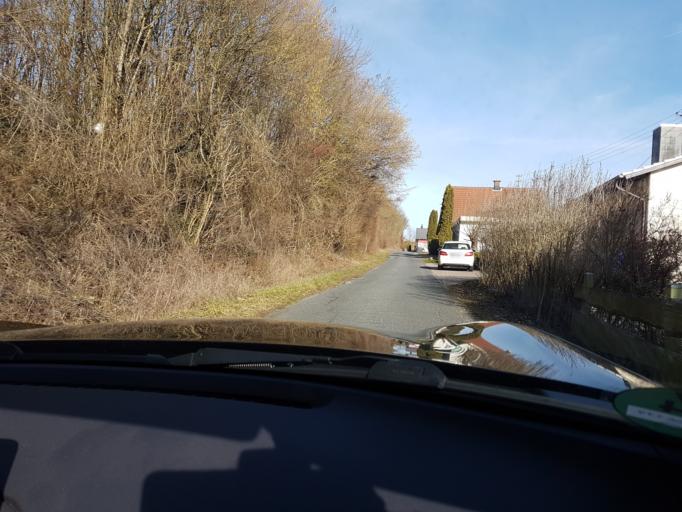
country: DE
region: Baden-Wuerttemberg
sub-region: Karlsruhe Region
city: Osterburken
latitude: 49.4355
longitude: 9.4268
